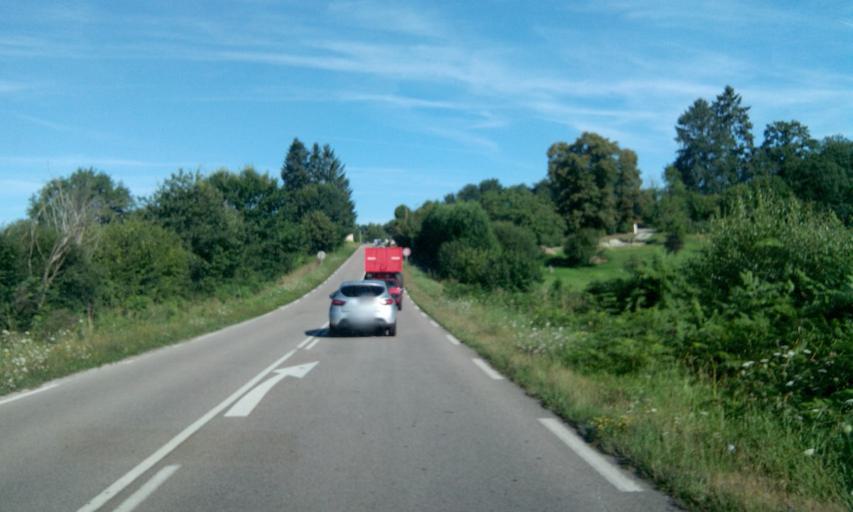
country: FR
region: Limousin
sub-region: Departement de la Haute-Vienne
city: Saint-Leonard-de-Noblat
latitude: 45.8444
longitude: 1.4604
